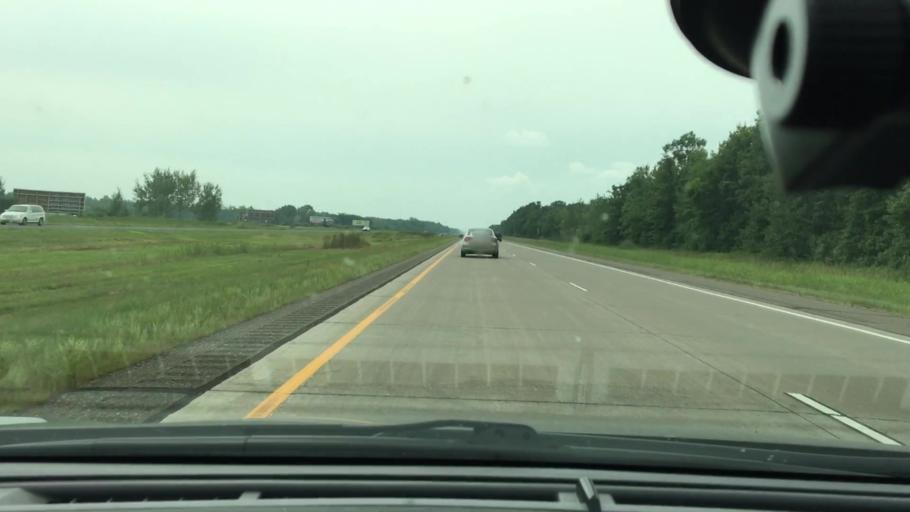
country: US
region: Minnesota
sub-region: Mille Lacs County
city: Vineland
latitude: 46.0349
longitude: -93.6630
